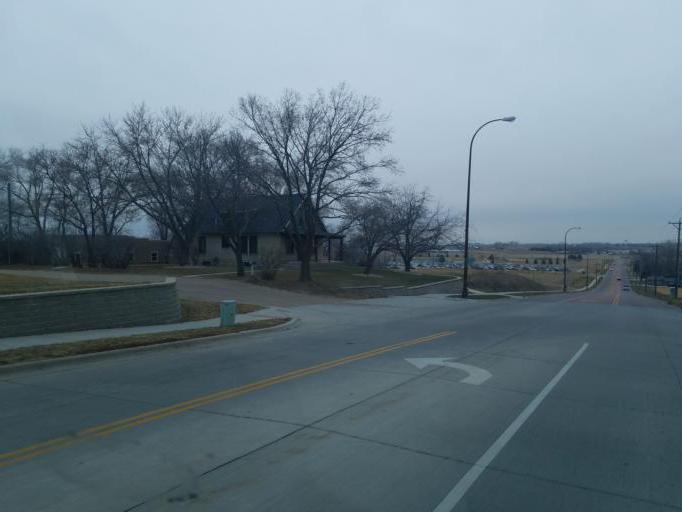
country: US
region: South Dakota
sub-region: Yankton County
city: Yankton
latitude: 42.8832
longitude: -97.4072
